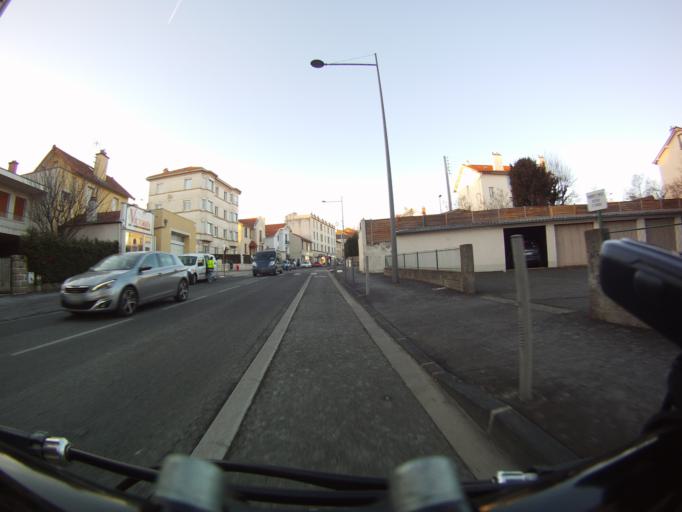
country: FR
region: Auvergne
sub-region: Departement du Puy-de-Dome
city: Clermont-Ferrand
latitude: 45.7653
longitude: 3.0971
